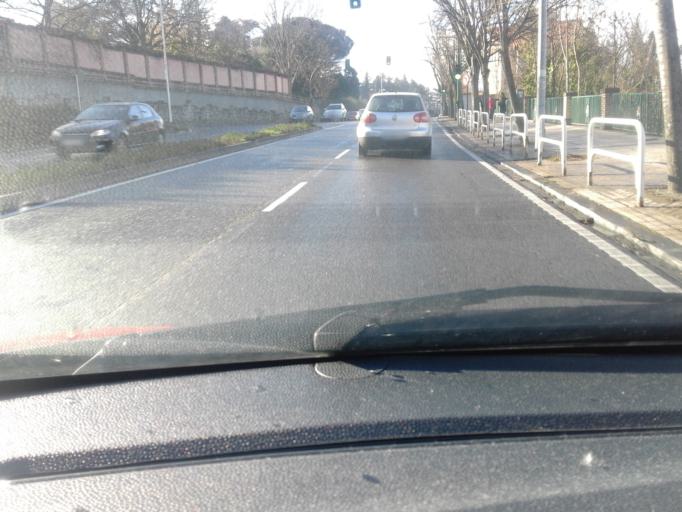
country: ES
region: Navarre
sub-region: Provincia de Navarra
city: Burlata
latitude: 42.8153
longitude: -1.6270
